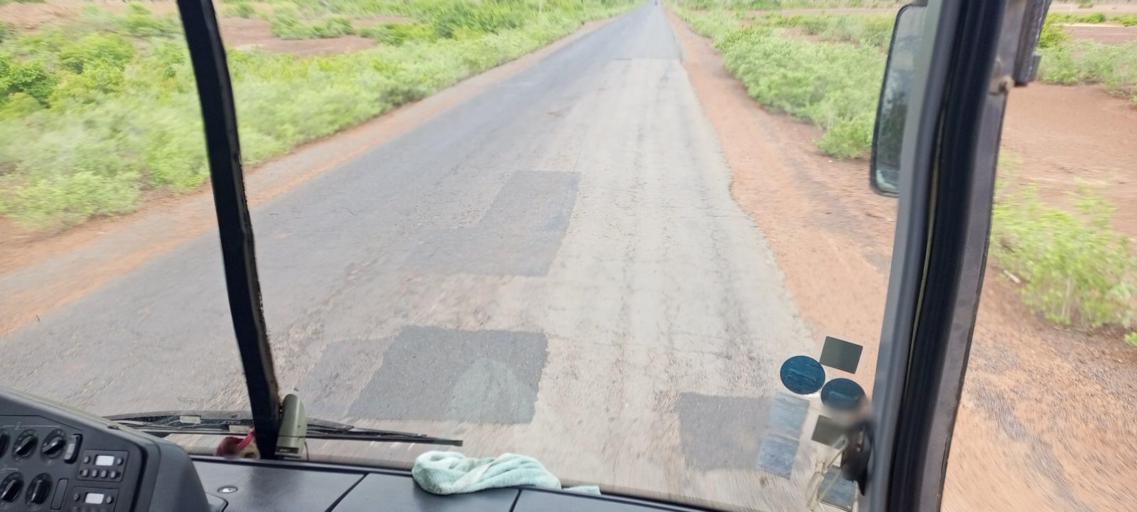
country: ML
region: Segou
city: Bla
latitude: 12.7519
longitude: -5.7339
